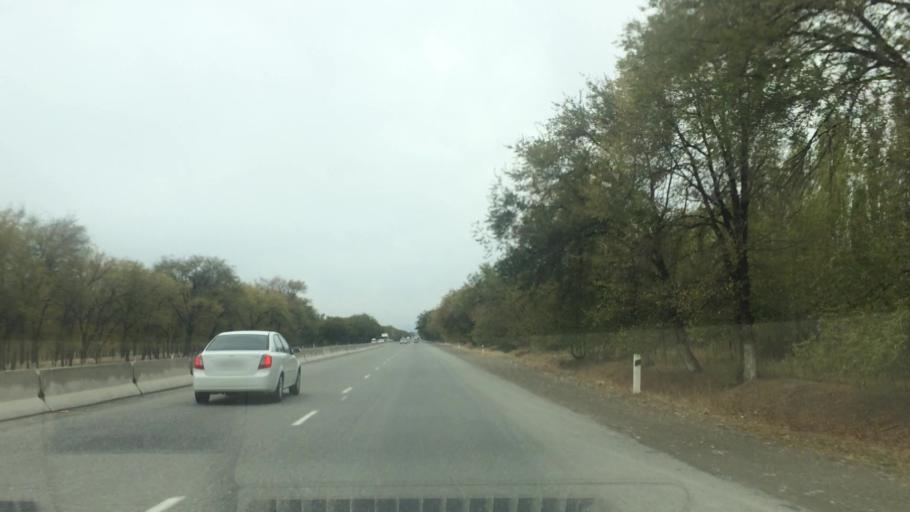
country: UZ
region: Samarqand
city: Bulung'ur
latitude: 39.8014
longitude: 67.3449
